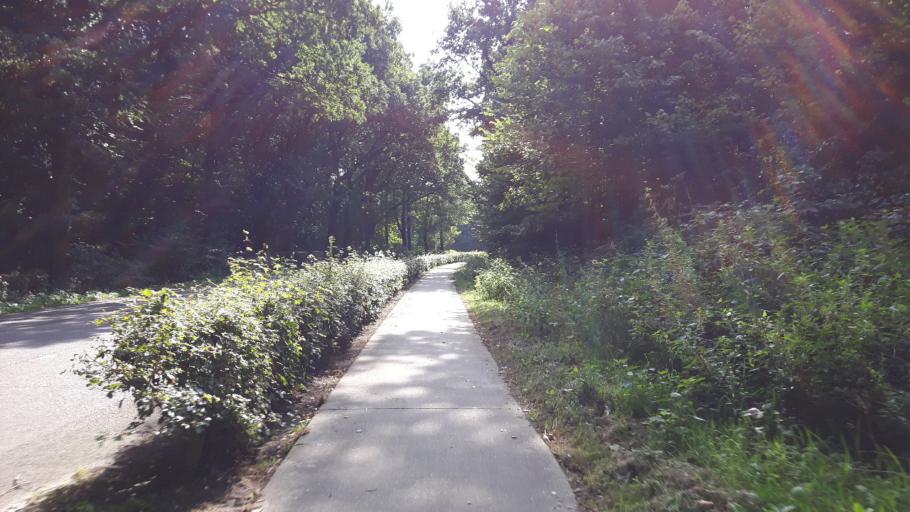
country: NL
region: Groningen
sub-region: Gemeente Leek
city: Leek
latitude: 53.1212
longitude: 6.4472
